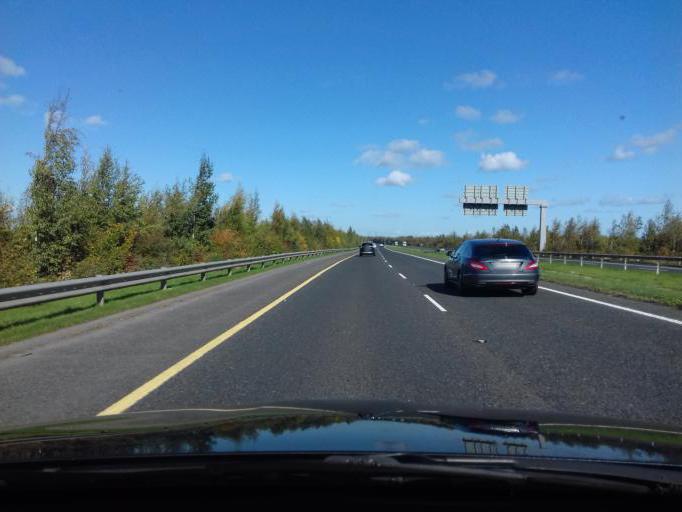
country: IE
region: Leinster
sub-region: Fingal County
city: Blanchardstown
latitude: 53.4475
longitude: -6.3554
